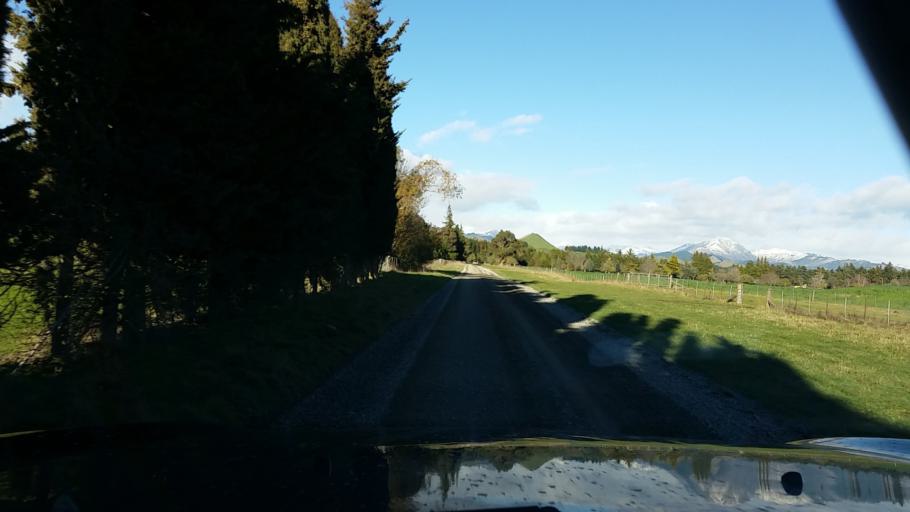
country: NZ
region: Marlborough
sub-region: Marlborough District
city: Blenheim
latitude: -41.6159
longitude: 173.6863
